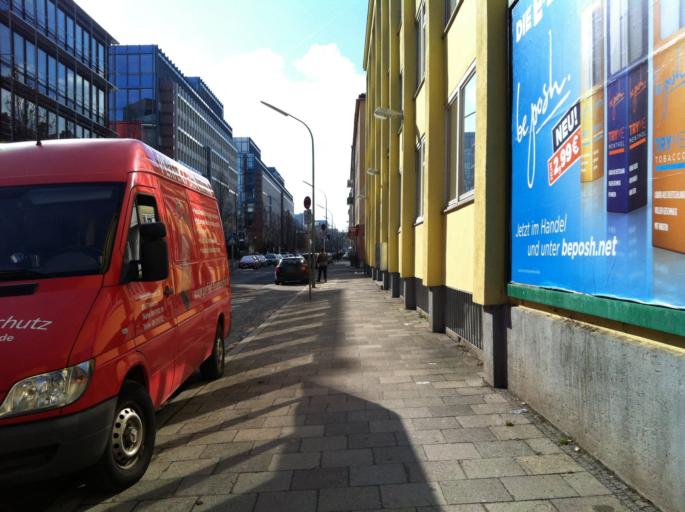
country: DE
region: Bavaria
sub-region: Upper Bavaria
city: Pullach im Isartal
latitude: 48.0988
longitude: 11.5333
